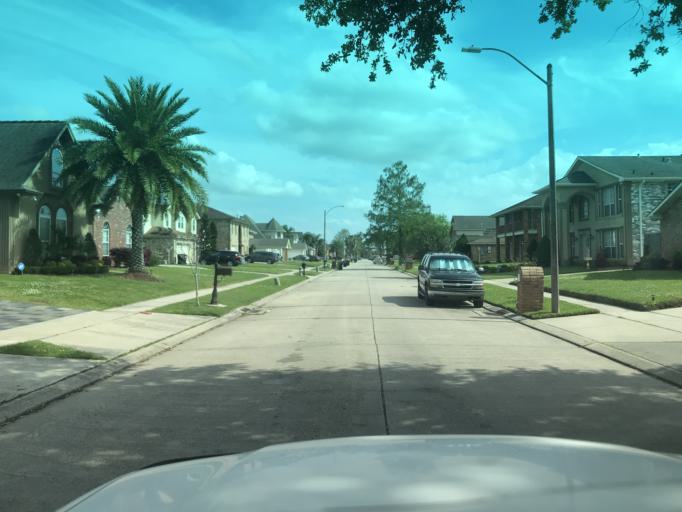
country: US
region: Louisiana
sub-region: Saint Bernard Parish
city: Chalmette
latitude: 30.0351
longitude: -89.9564
